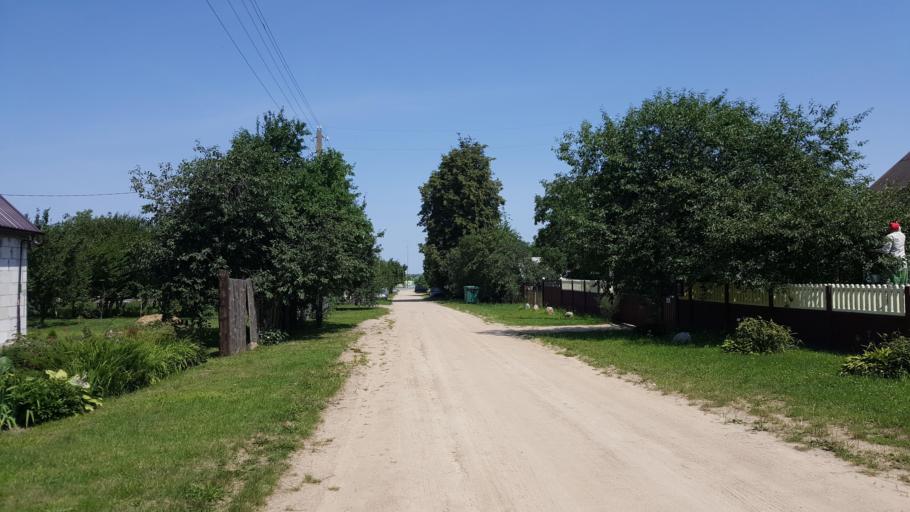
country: BY
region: Brest
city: Vysokaye
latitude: 52.3600
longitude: 23.4024
